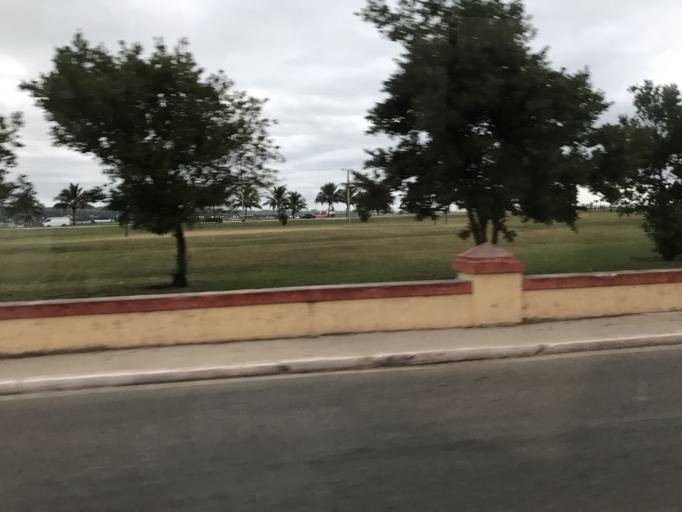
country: CU
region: Matanzas
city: Matanzas
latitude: 23.0364
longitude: -81.5628
